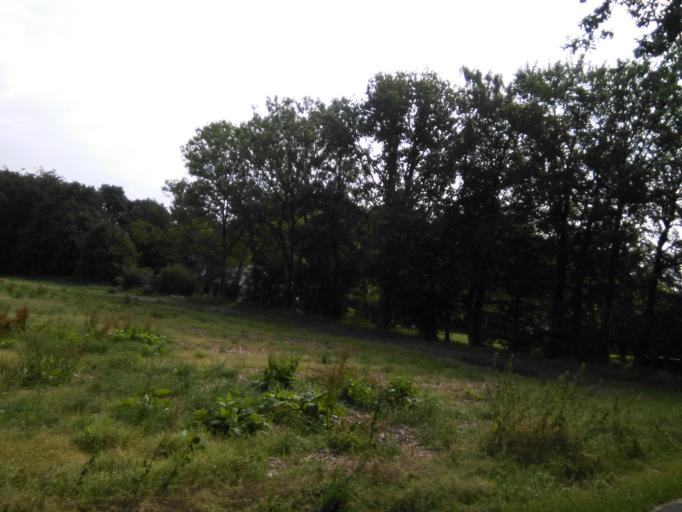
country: DK
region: Central Jutland
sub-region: Odder Kommune
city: Odder
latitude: 55.8831
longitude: 10.0553
